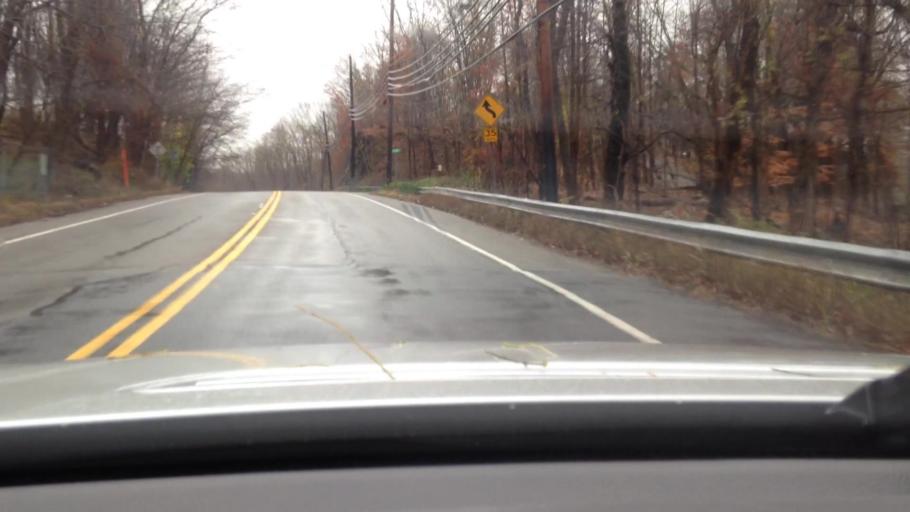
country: US
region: New York
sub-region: Westchester County
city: Peekskill
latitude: 41.3182
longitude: -73.9305
